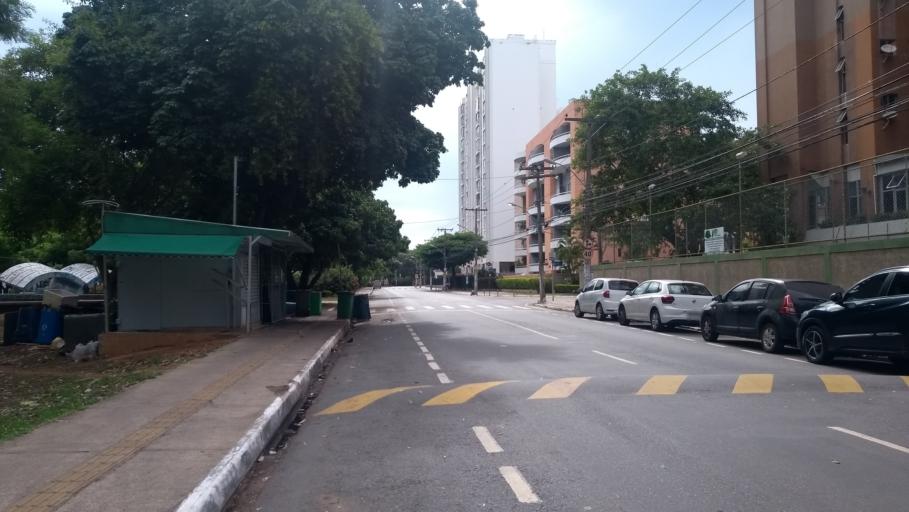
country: BR
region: Bahia
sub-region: Salvador
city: Salvador
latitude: -12.9934
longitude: -38.4624
